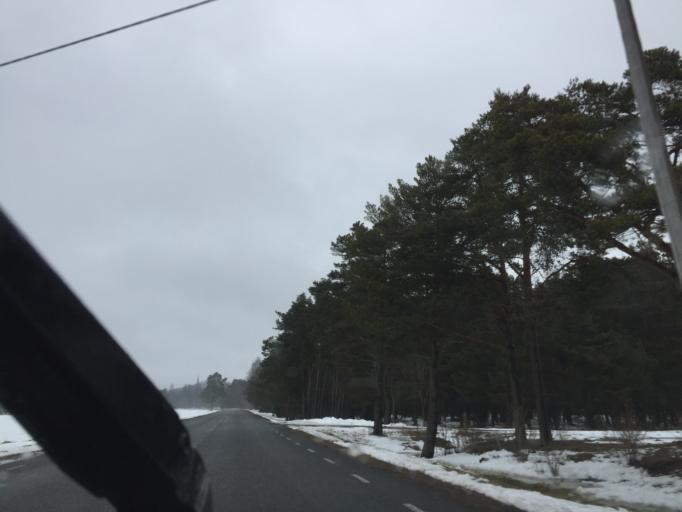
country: EE
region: Saare
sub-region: Kuressaare linn
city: Kuressaare
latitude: 58.3490
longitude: 22.0323
